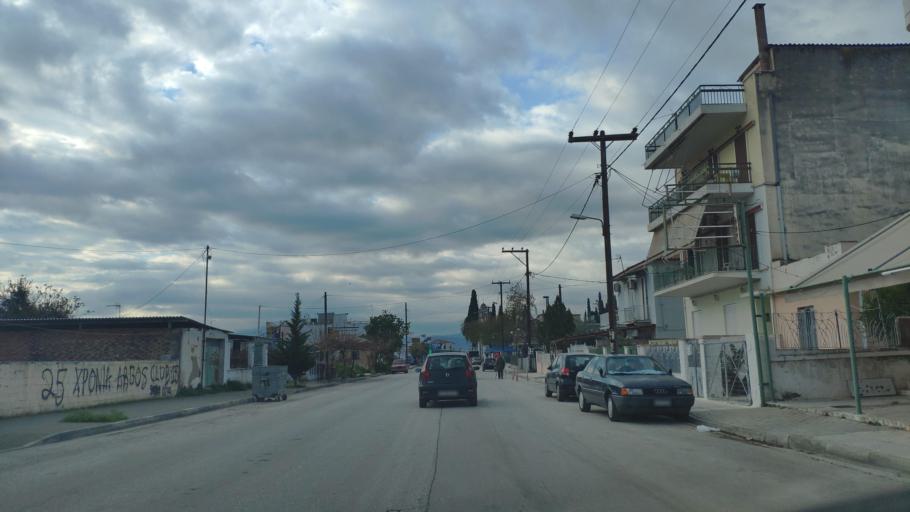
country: GR
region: Peloponnese
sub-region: Nomos Argolidos
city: Argos
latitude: 37.6301
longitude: 22.7205
